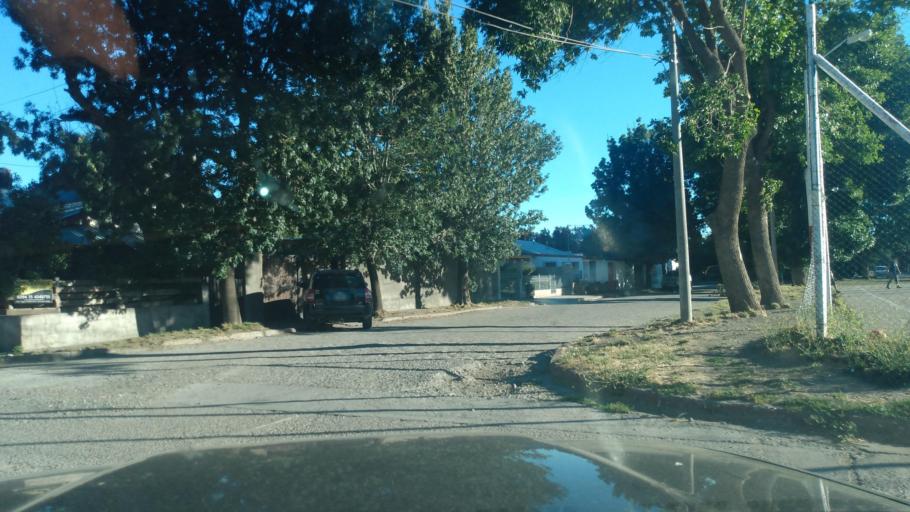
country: AR
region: Neuquen
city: Junin de los Andes
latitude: -39.9505
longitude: -71.0772
